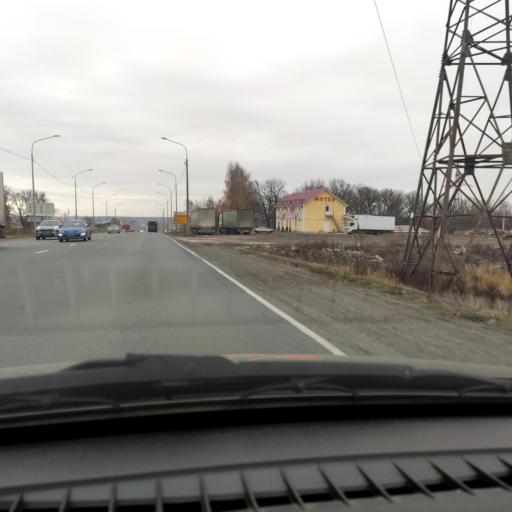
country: RU
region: Samara
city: Zhigulevsk
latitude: 53.3789
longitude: 49.4562
